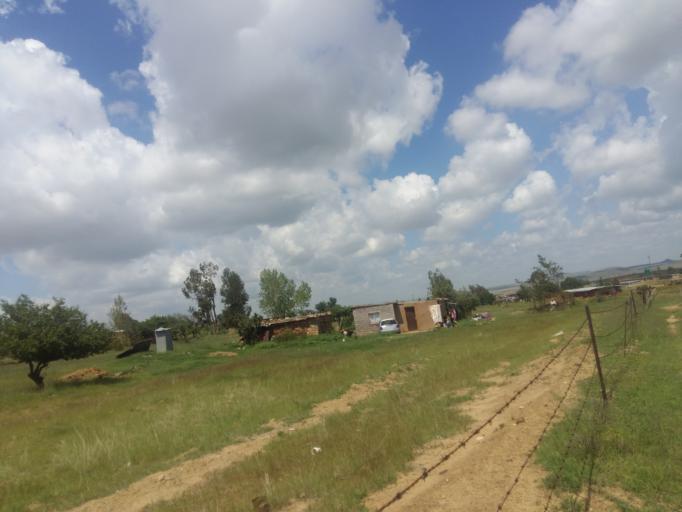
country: LS
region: Mafeteng
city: Mafeteng
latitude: -29.7526
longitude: 27.1137
